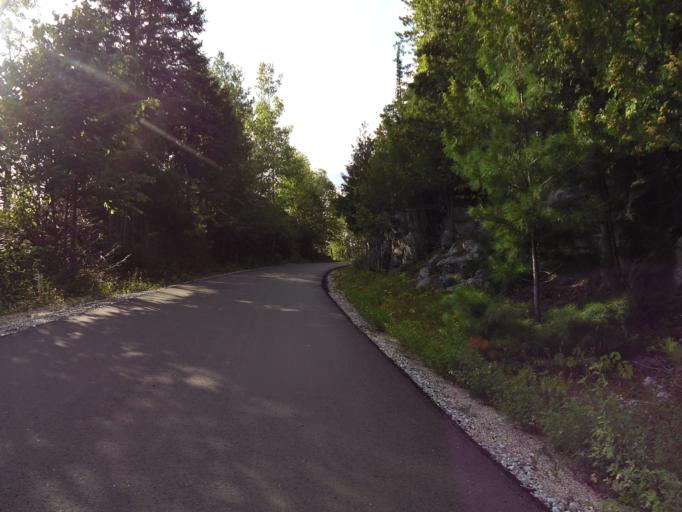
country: CA
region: Quebec
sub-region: Outaouais
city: Maniwaki
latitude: 46.2140
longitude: -76.0430
